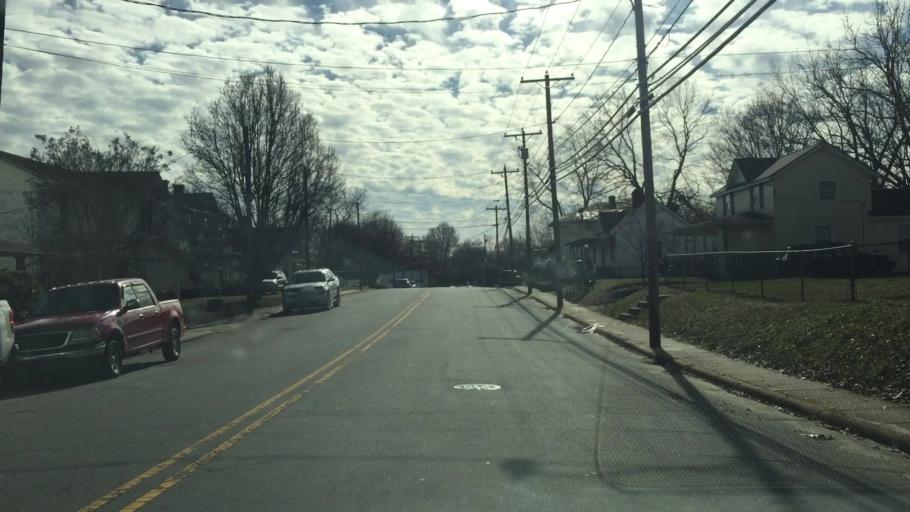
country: US
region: North Carolina
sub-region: Rockingham County
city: Reidsville
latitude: 36.3552
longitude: -79.6560
